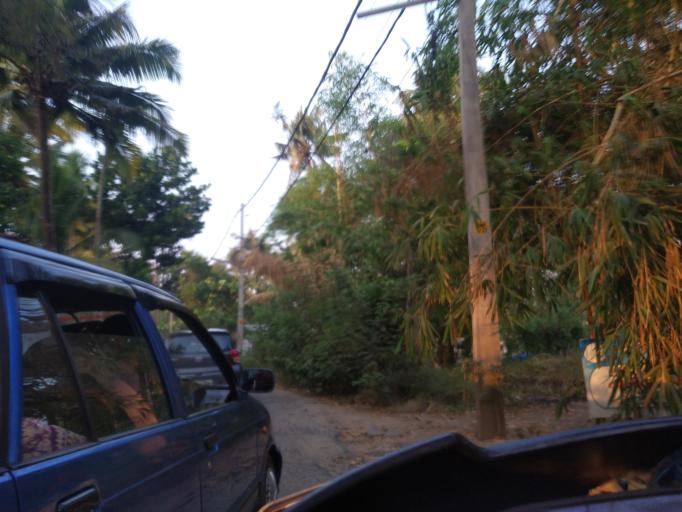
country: IN
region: Kerala
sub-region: Thrissur District
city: Kodungallur
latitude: 10.1751
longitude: 76.1666
